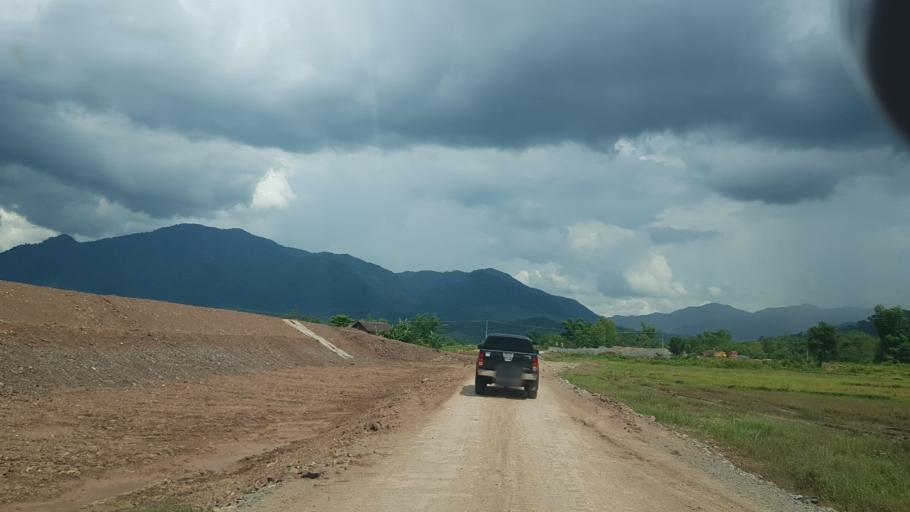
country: LA
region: Oudomxai
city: Muang Xay
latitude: 20.6796
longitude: 101.9692
